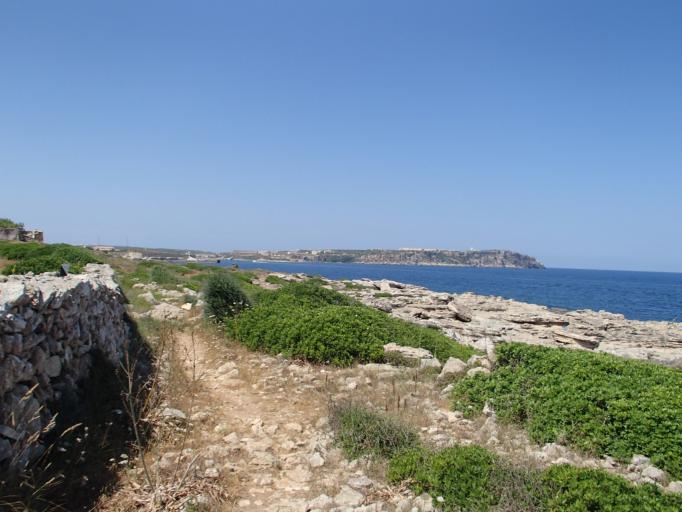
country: ES
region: Balearic Islands
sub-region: Illes Balears
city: Es Castell
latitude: 39.8560
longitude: 4.3060
